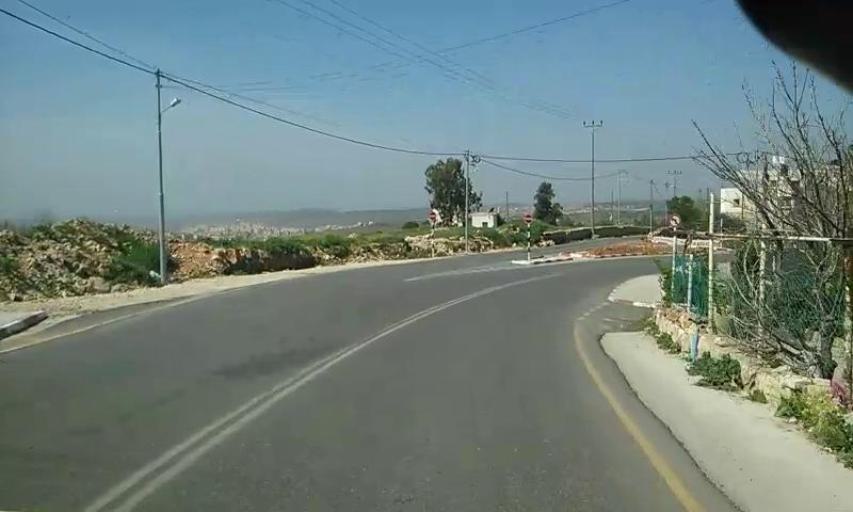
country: PS
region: West Bank
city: Husan
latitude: 31.7049
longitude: 35.1440
